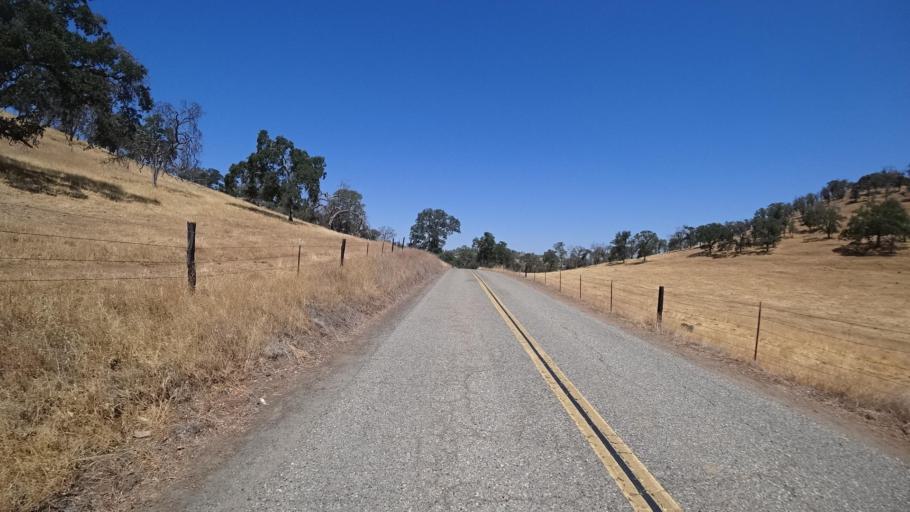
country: US
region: California
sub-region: Mariposa County
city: Mariposa
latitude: 37.2790
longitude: -119.9755
